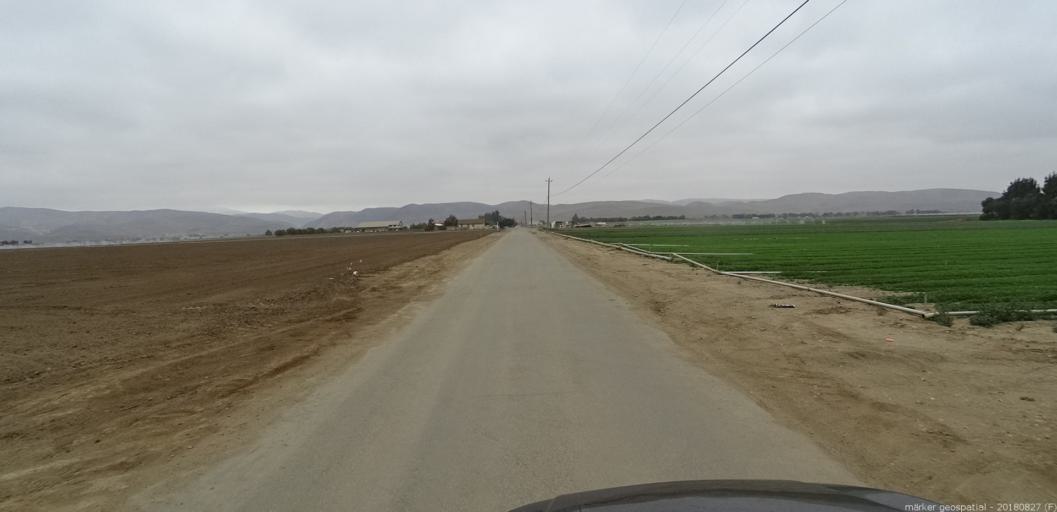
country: US
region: California
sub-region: Monterey County
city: Greenfield
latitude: 36.3313
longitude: -121.2252
